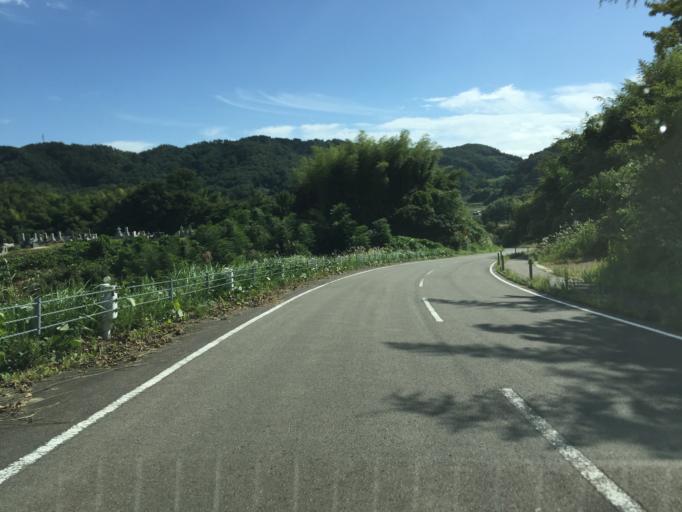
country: JP
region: Fukushima
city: Hobaramachi
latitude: 37.7776
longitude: 140.5411
